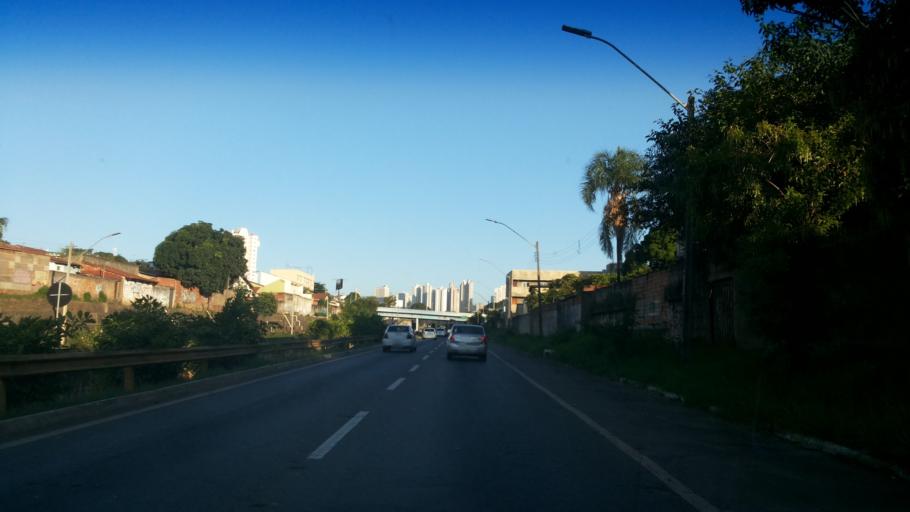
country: BR
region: Goias
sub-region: Goiania
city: Goiania
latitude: -16.6827
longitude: -49.2475
